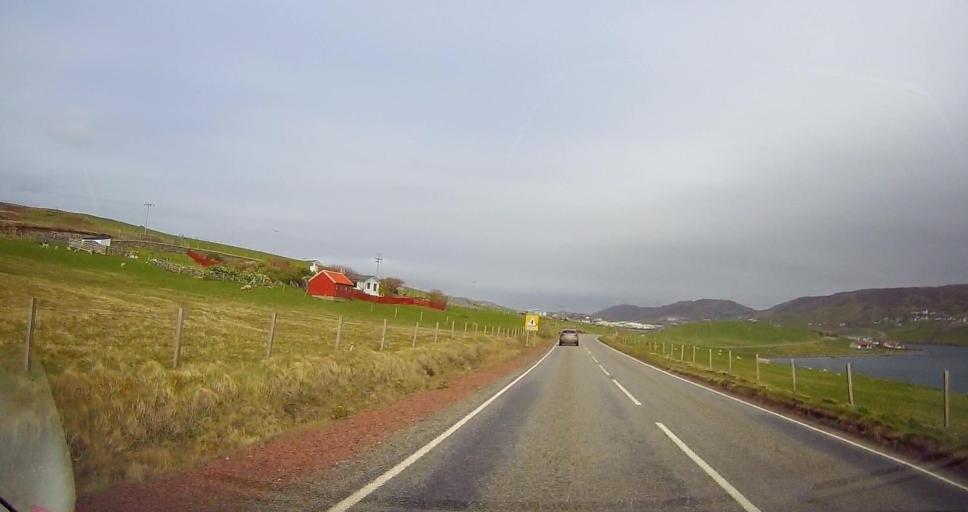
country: GB
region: Scotland
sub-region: Shetland Islands
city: Sandwick
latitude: 60.1231
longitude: -1.2868
